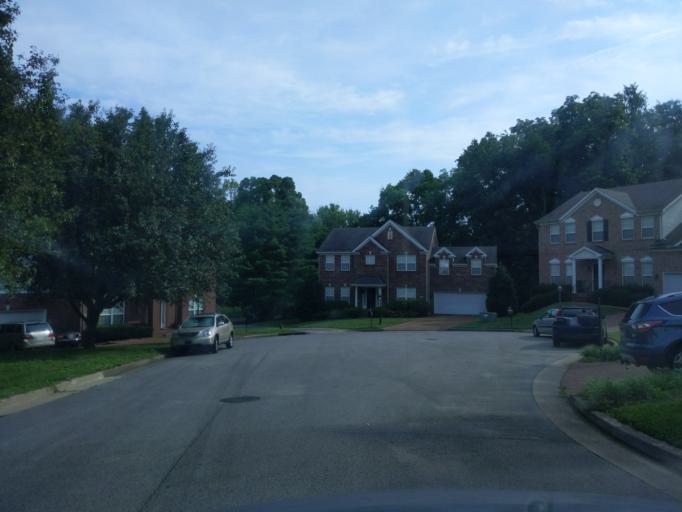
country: US
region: Tennessee
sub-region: Williamson County
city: Brentwood Estates
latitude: 36.0251
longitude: -86.7526
